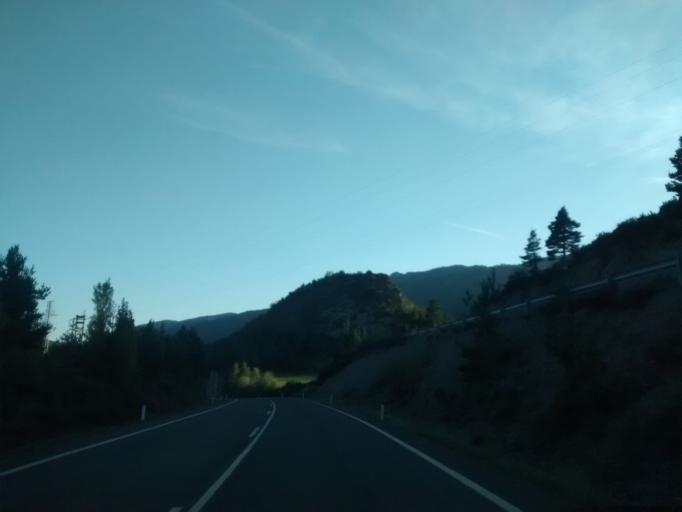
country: ES
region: Aragon
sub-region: Provincia de Huesca
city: Anso
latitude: 42.7289
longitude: -0.7534
